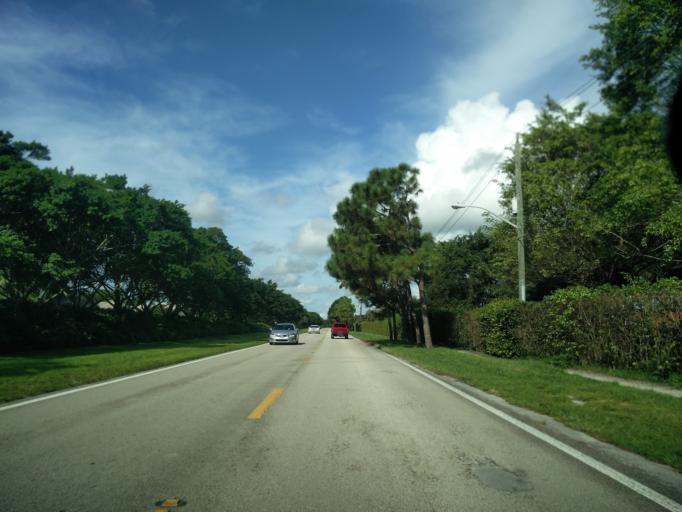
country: US
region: Florida
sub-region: Broward County
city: Pine Island Ridge
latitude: 26.0904
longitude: -80.2675
